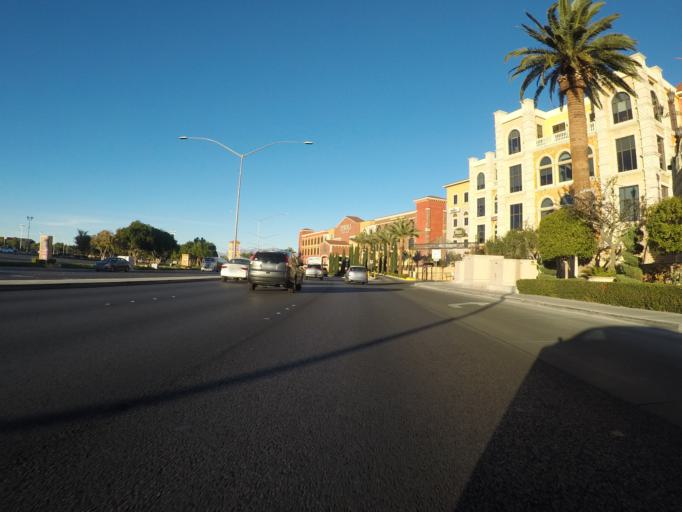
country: US
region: Nevada
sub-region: Clark County
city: Summerlin South
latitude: 36.1670
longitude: -115.2876
